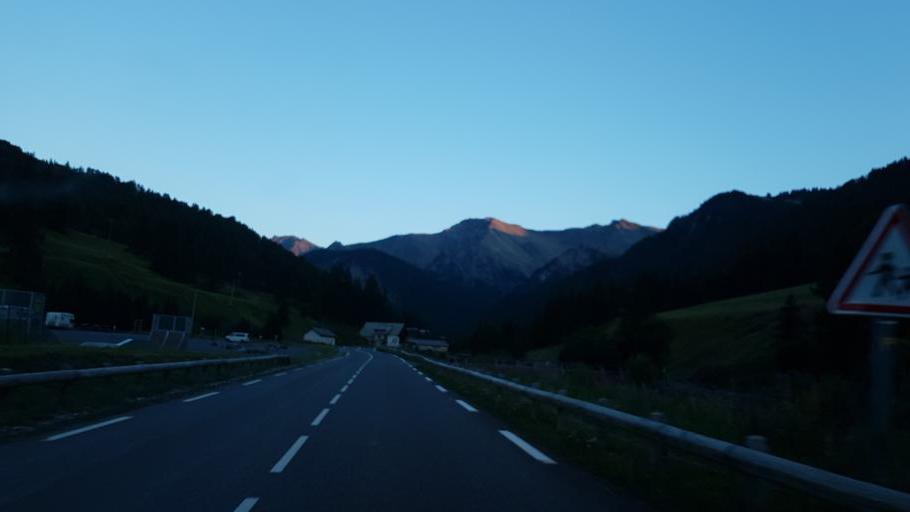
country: FR
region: Provence-Alpes-Cote d'Azur
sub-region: Departement des Hautes-Alpes
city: Guillestre
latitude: 44.7200
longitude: 6.8466
